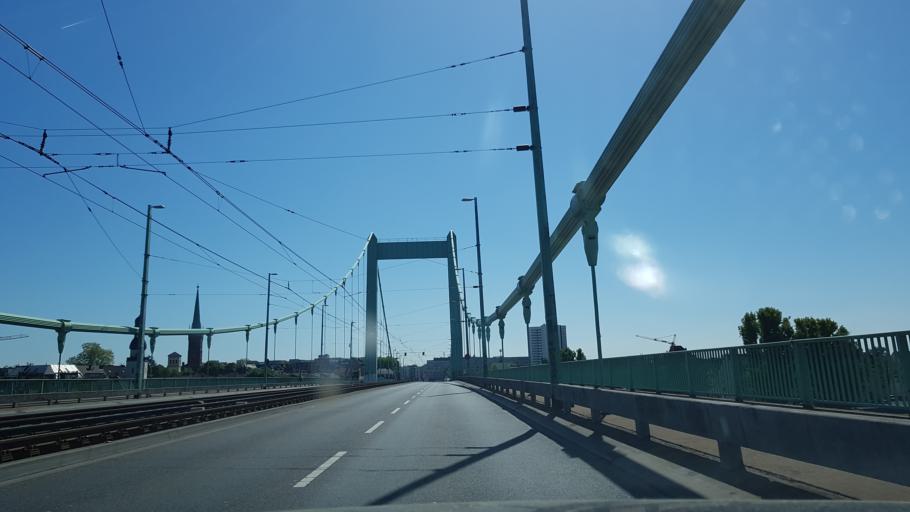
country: DE
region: North Rhine-Westphalia
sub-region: Regierungsbezirk Koln
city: Muelheim
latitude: 50.9644
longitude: 6.9949
